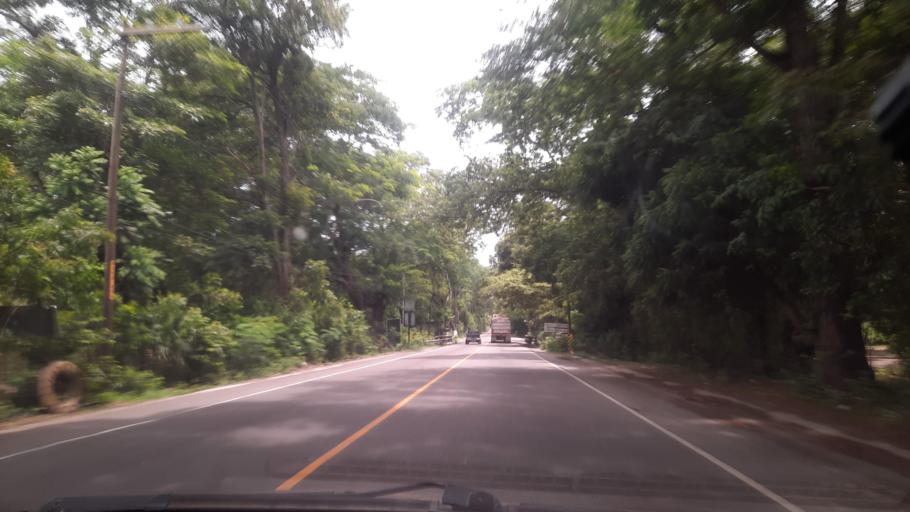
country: GT
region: Zacapa
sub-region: Municipio de Zacapa
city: Gualan
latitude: 15.0899
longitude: -89.4461
